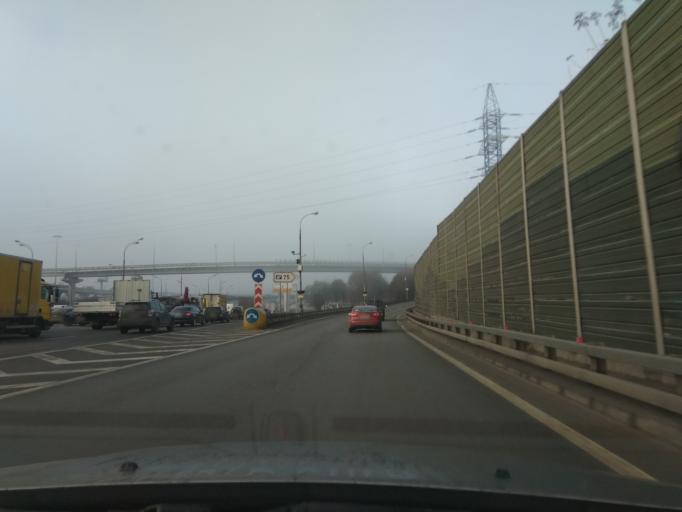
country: RU
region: Moscow
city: Khimki
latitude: 55.8828
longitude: 37.4501
